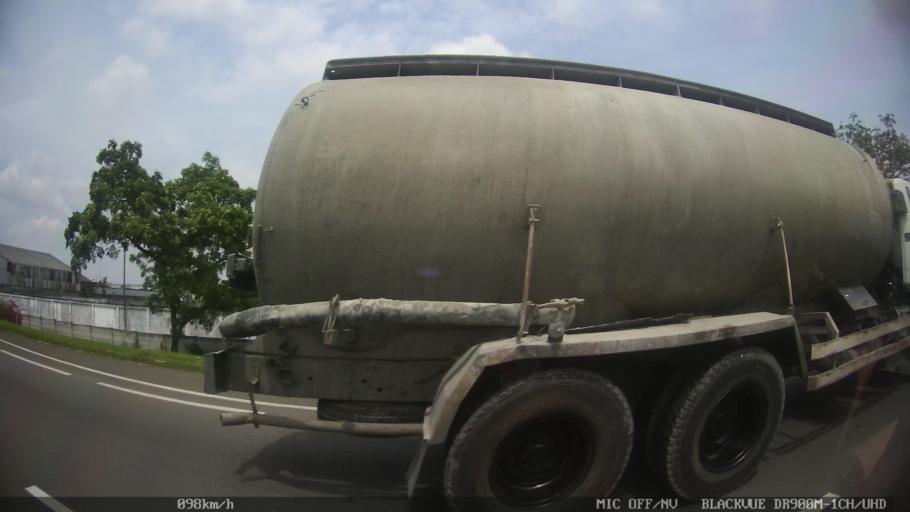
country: ID
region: North Sumatra
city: Labuhan Deli
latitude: 3.6763
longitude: 98.6802
